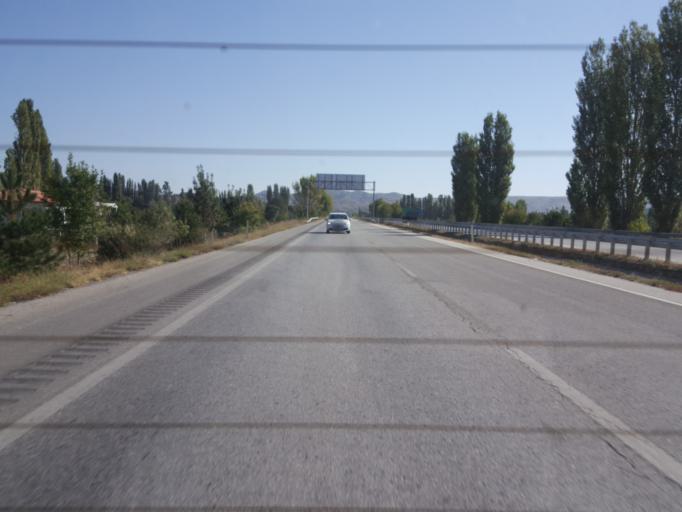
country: TR
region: Corum
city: Sungurlu
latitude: 40.1784
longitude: 34.4660
